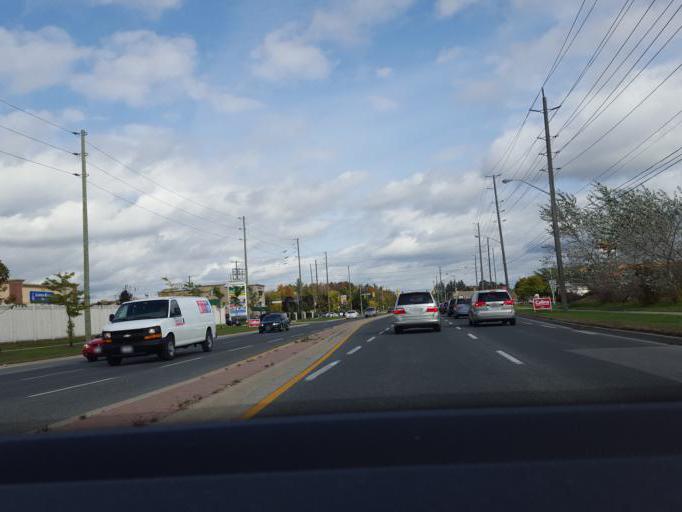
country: CA
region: Ontario
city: Oshawa
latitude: 43.9212
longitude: -78.9304
